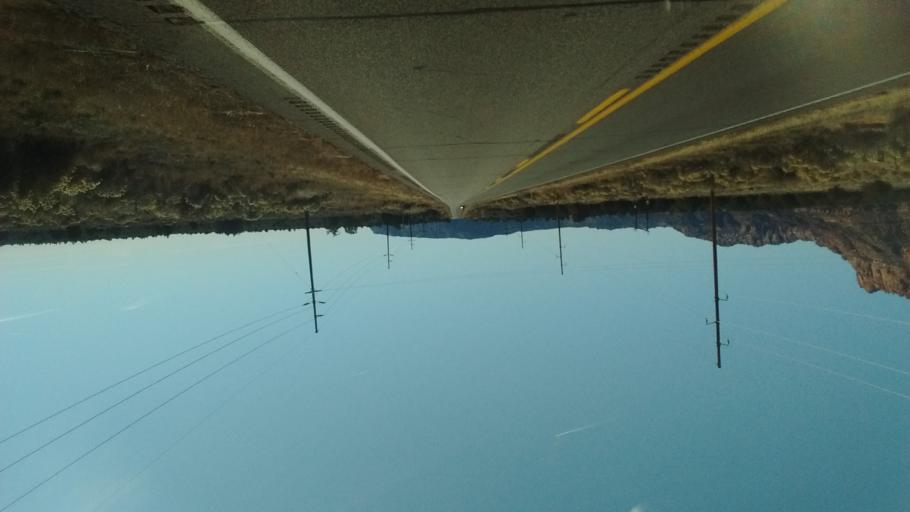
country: US
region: Arizona
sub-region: Mohave County
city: Colorado City
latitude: 37.0266
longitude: -113.0484
